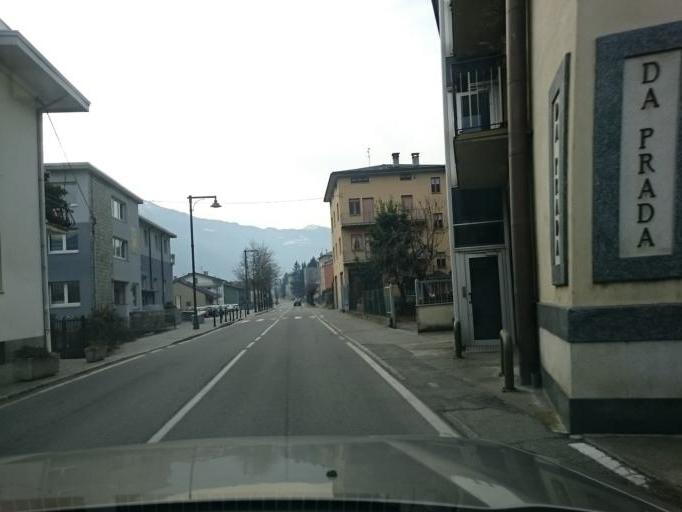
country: IT
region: Lombardy
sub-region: Provincia di Sondrio
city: Grosotto
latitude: 46.2792
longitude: 10.2585
